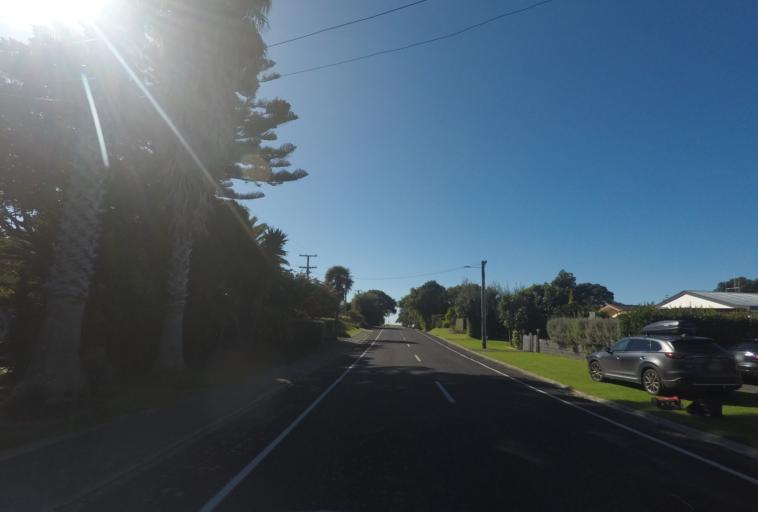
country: NZ
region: Waikato
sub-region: Thames-Coromandel District
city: Whangamata
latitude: -37.2832
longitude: 175.8997
